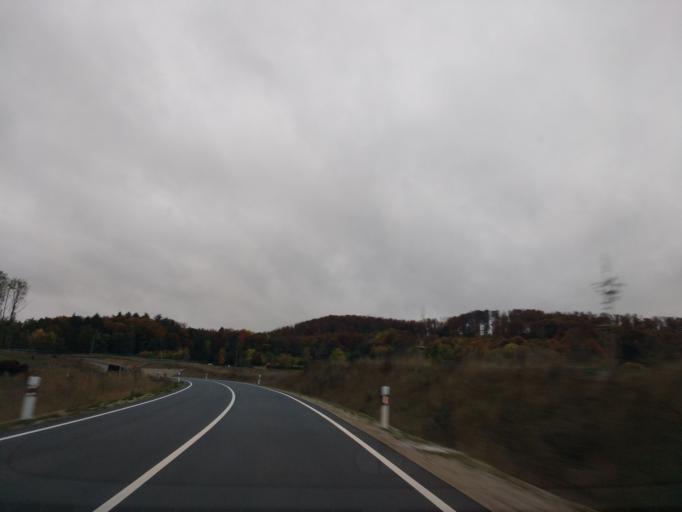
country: DE
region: Thuringia
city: Buhla
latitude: 51.4408
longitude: 10.4442
